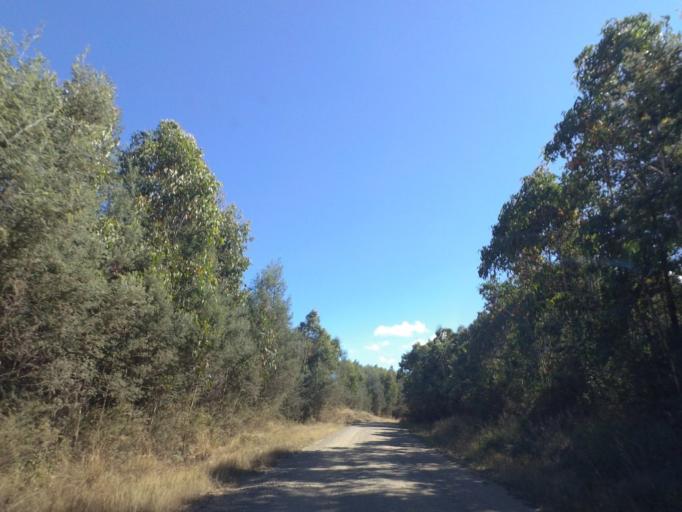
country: AU
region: Victoria
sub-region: Murrindindi
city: Alexandra
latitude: -37.4106
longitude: 145.8063
